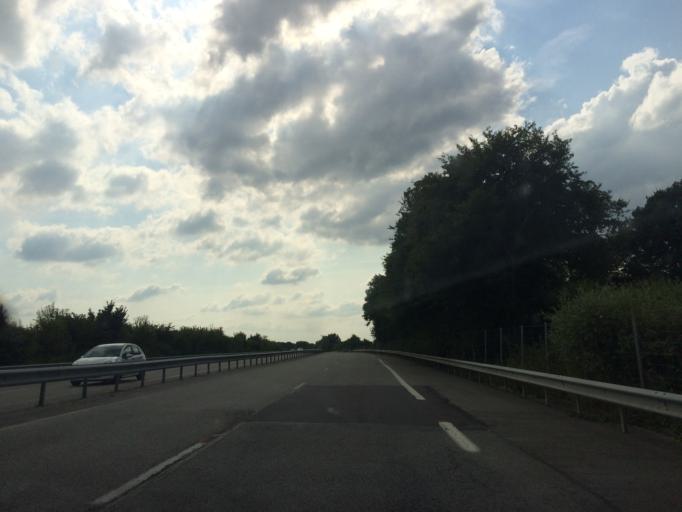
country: FR
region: Pays de la Loire
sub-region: Departement de la Sarthe
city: Mamers
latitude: 48.5052
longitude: 0.3158
